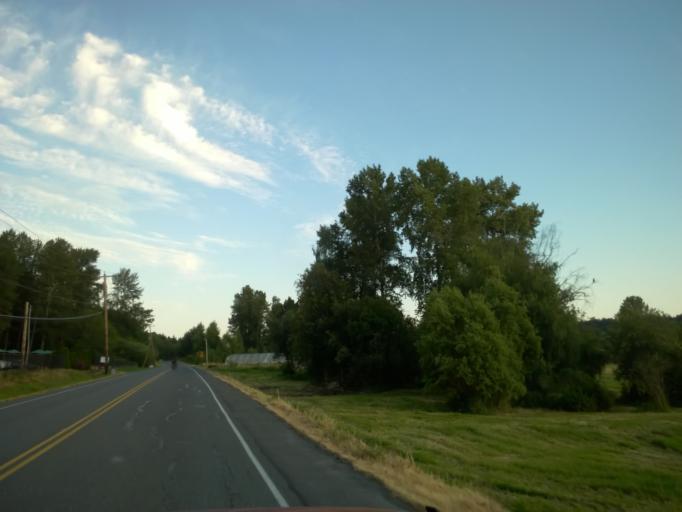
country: US
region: Washington
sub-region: King County
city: Woodinville
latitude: 47.7443
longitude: -122.1472
